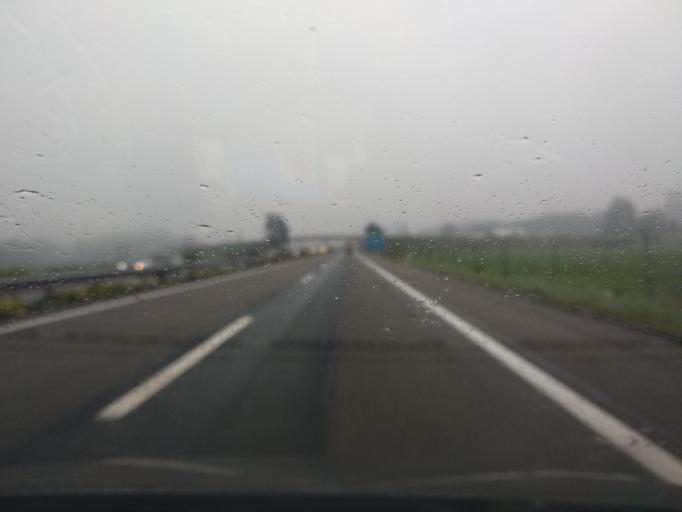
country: CH
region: Saint Gallen
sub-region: Wahlkreis Wil
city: Uzwil
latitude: 47.4533
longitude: 9.1398
